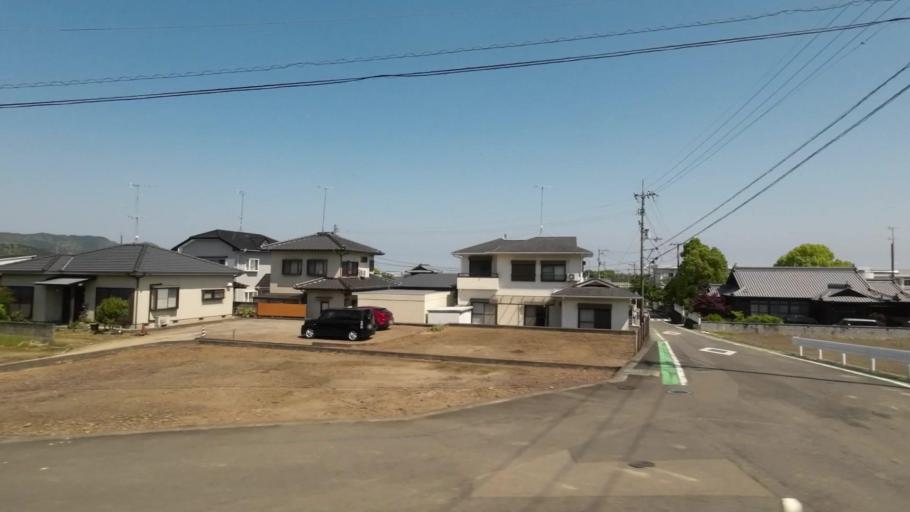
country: JP
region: Ehime
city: Niihama
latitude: 33.9612
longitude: 133.4363
